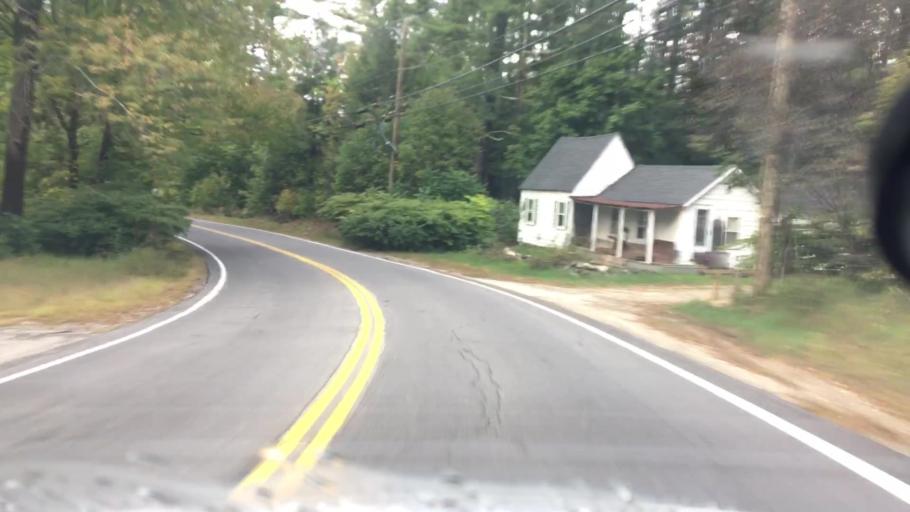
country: US
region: New Hampshire
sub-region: Carroll County
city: Wakefield
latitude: 43.5613
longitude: -71.0280
